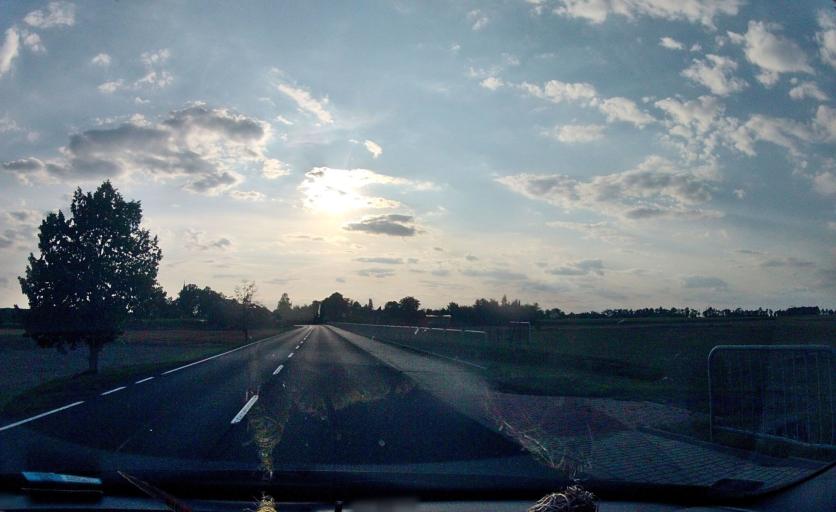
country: PL
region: Opole Voivodeship
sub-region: Powiat oleski
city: Gorzow Slaski
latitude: 51.0022
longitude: 18.3222
